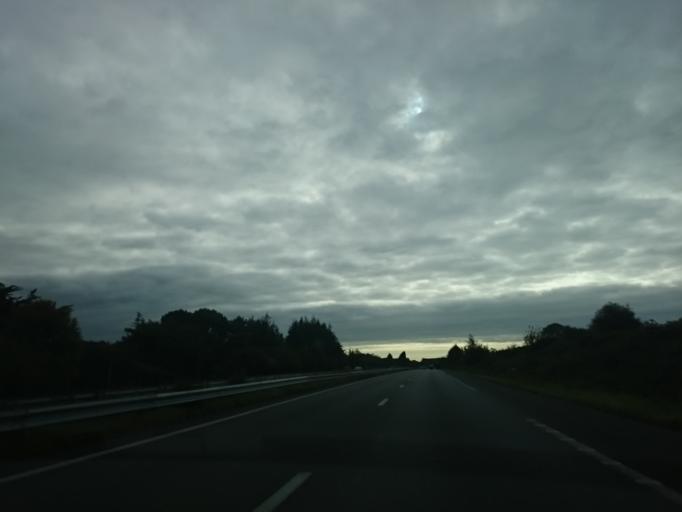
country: FR
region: Brittany
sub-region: Departement du Morbihan
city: Landaul
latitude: 47.7223
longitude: -3.0732
